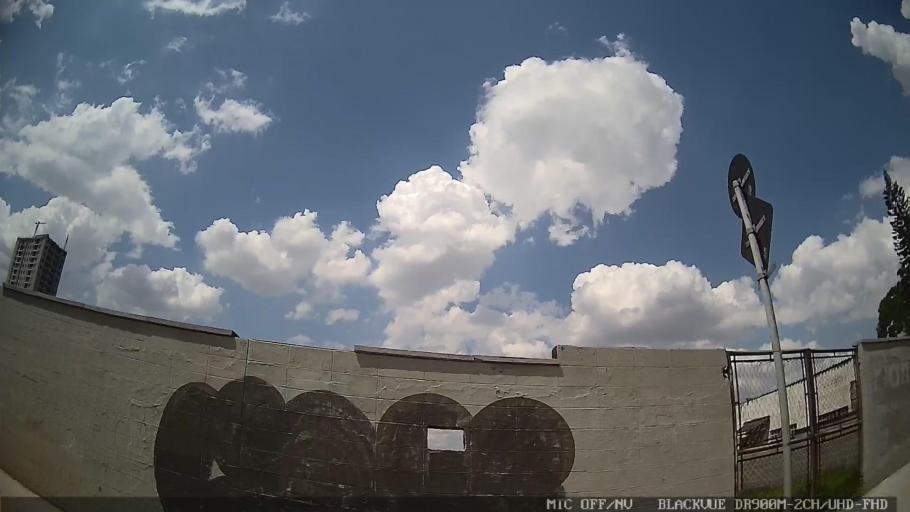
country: BR
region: Sao Paulo
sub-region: Ferraz De Vasconcelos
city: Ferraz de Vasconcelos
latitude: -23.5419
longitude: -46.4509
